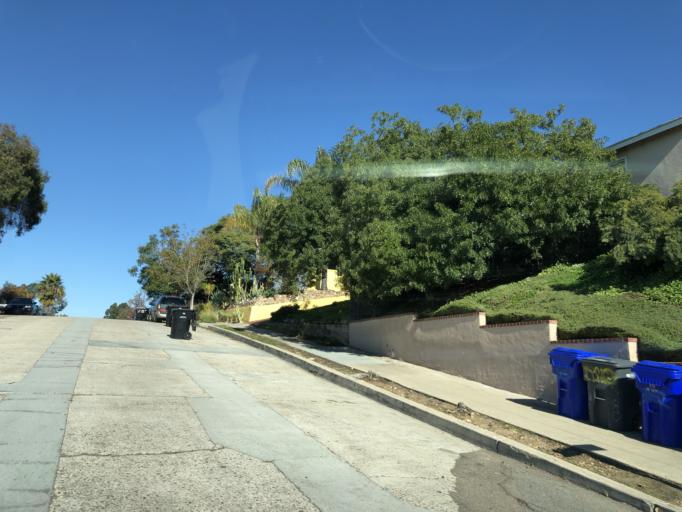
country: US
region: California
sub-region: San Diego County
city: San Diego
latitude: 32.7224
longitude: -117.1266
